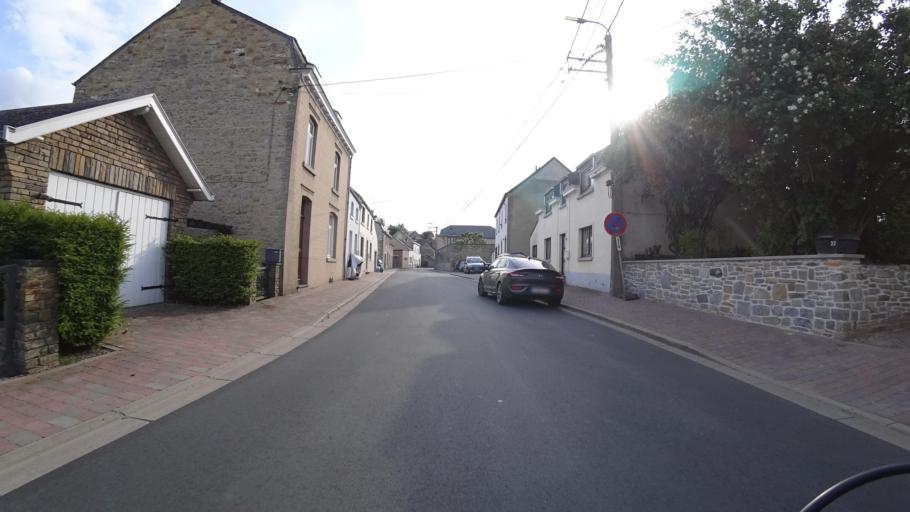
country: BE
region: Wallonia
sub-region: Province de Namur
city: Namur
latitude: 50.5071
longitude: 4.8074
